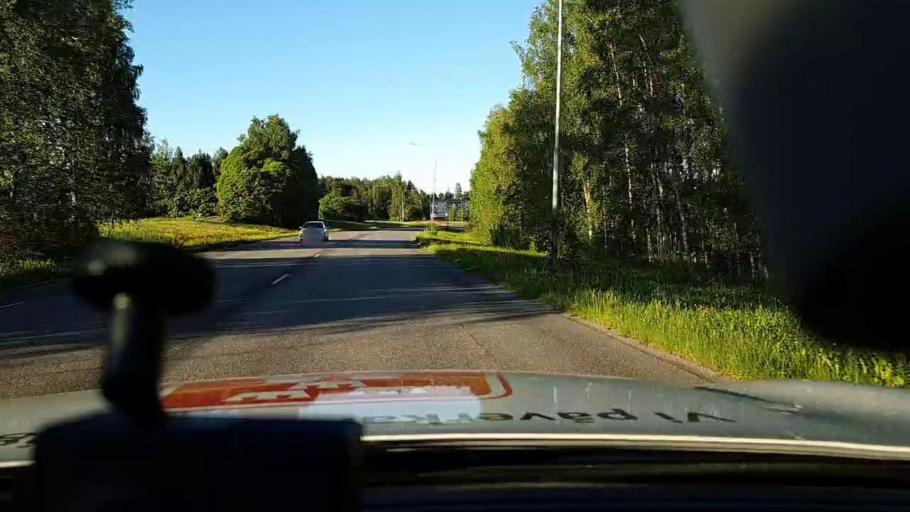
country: SE
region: Norrbotten
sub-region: Lulea Kommun
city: Lulea
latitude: 65.6142
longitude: 22.1430
